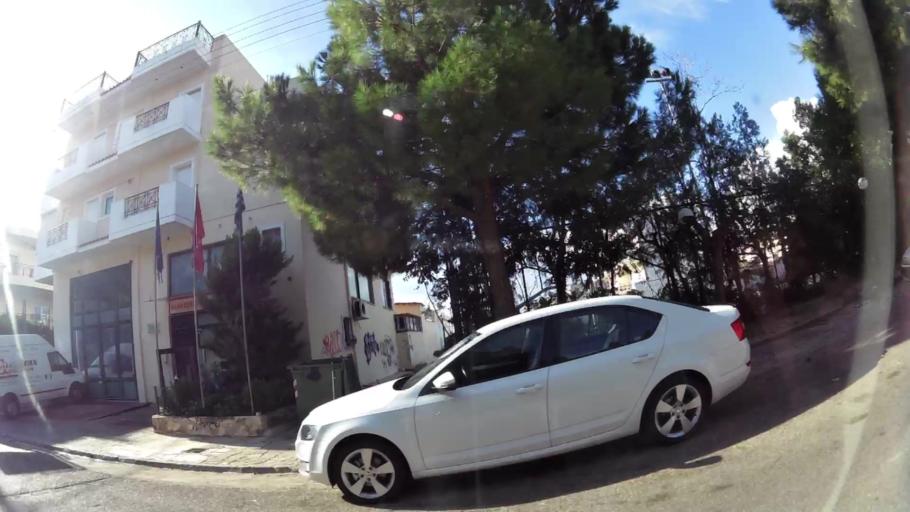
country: GR
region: Attica
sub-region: Nomarchia Athinas
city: Melissia
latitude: 38.0493
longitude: 23.8194
